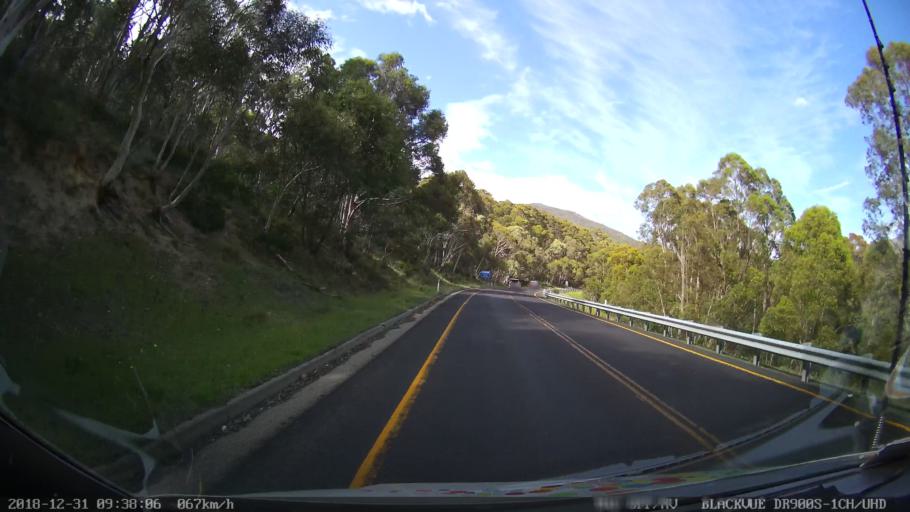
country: AU
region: New South Wales
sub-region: Snowy River
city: Jindabyne
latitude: -36.4720
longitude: 148.3709
